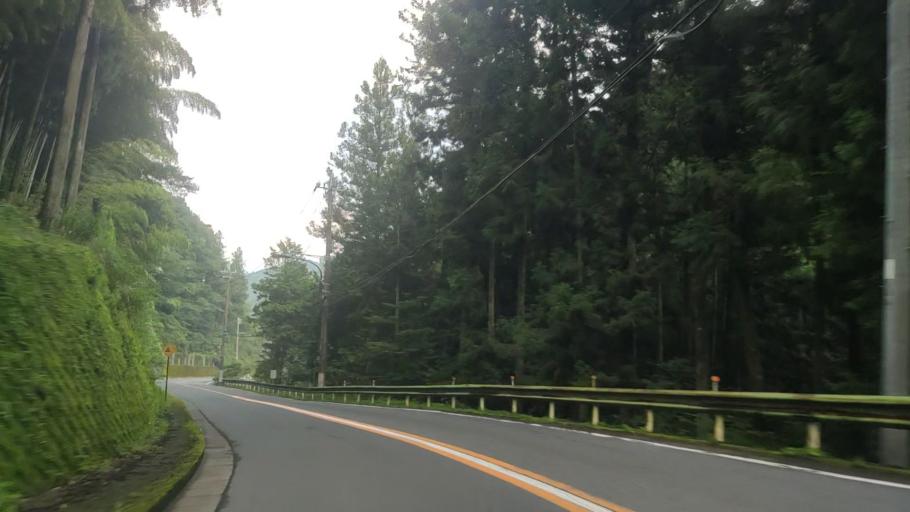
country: JP
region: Tokyo
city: Ome
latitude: 35.8345
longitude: 139.2201
